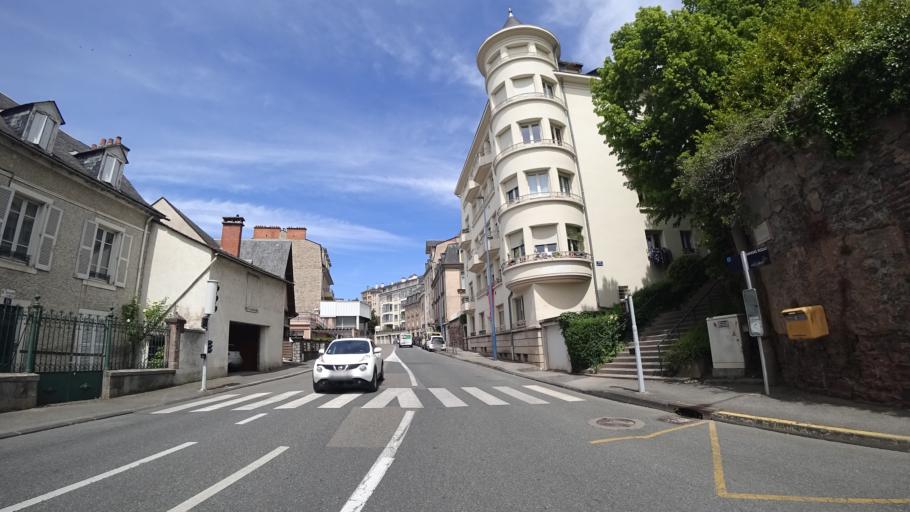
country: FR
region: Midi-Pyrenees
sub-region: Departement de l'Aveyron
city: Rodez
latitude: 44.3499
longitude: 2.5681
